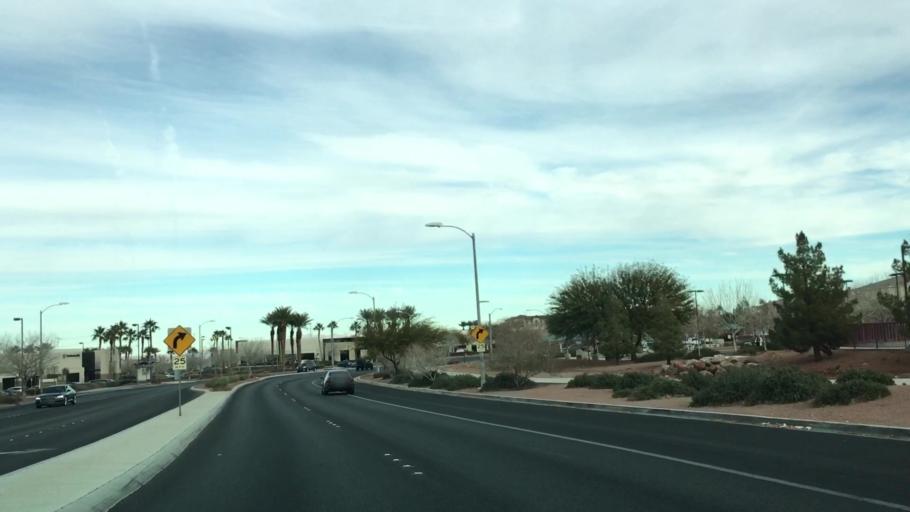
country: US
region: Nevada
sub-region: Clark County
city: Whitney
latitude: 36.0187
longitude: -115.0991
